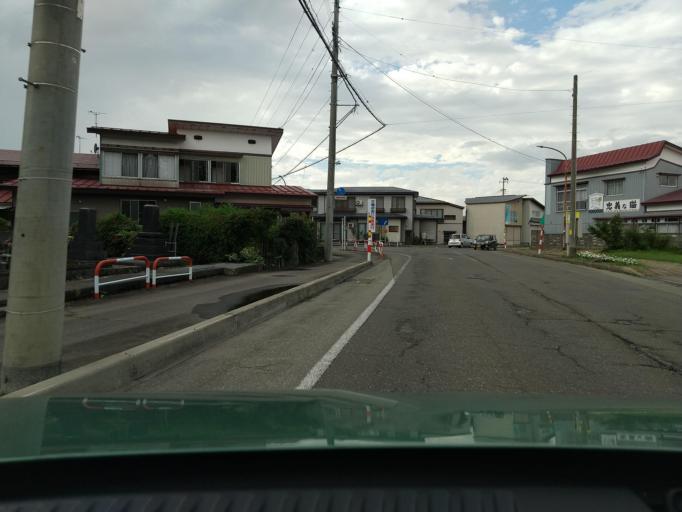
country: JP
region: Akita
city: Yokotemachi
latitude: 39.2603
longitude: 140.4906
